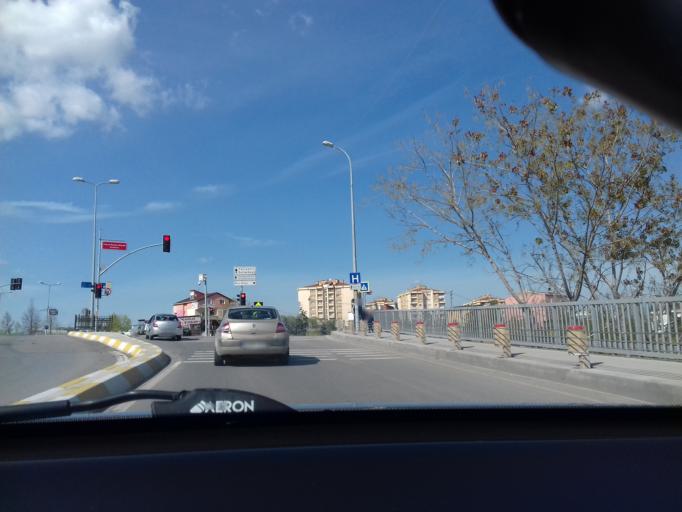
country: TR
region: Istanbul
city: Pendik
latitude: 40.9174
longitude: 29.2862
